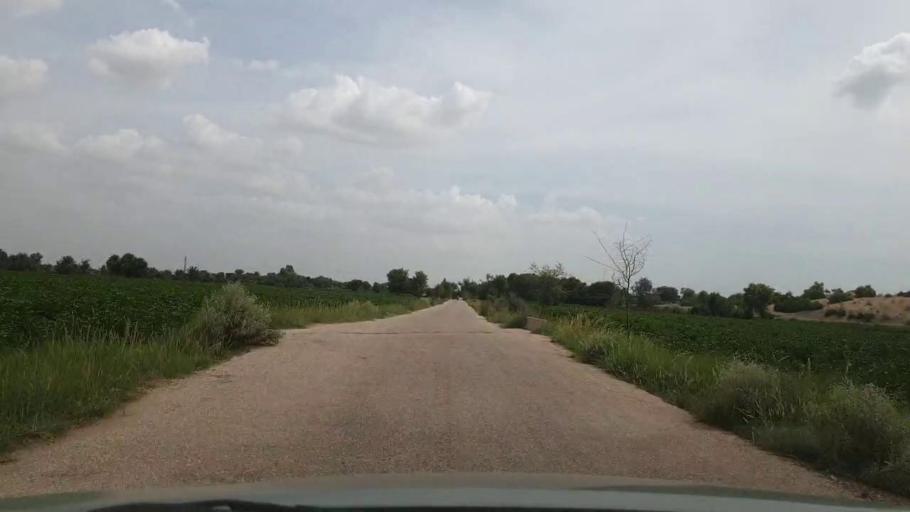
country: PK
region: Sindh
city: Kot Diji
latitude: 27.1595
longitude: 69.0351
